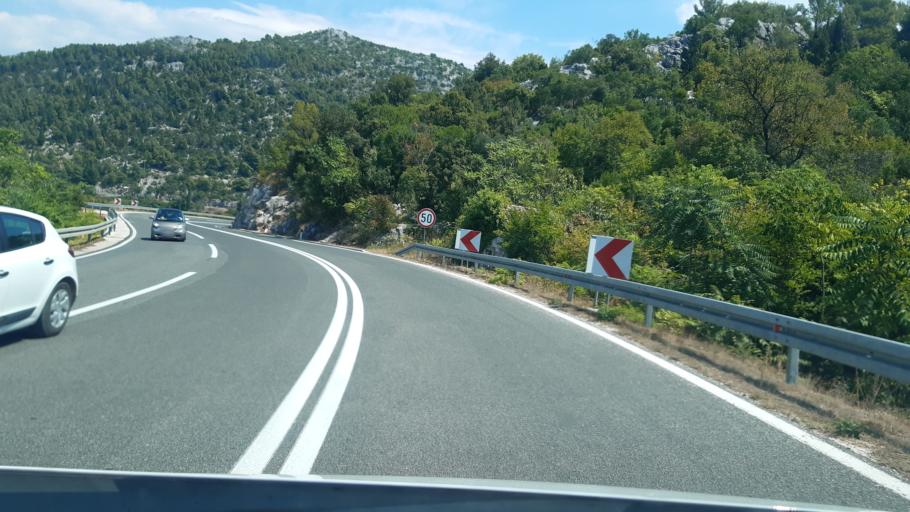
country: HR
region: Dubrovacko-Neretvanska
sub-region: Grad Dubrovnik
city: Opuzen
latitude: 42.9978
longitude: 17.5466
